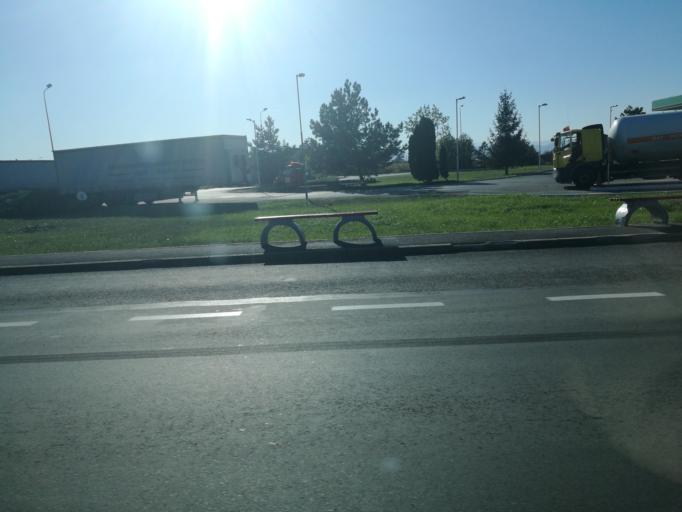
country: RO
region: Brasov
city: Brasov
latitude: 45.6841
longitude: 25.5835
